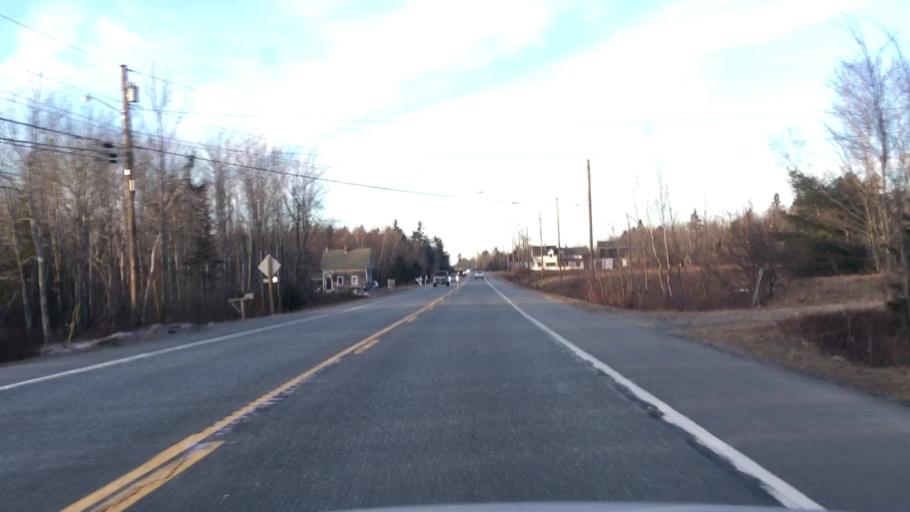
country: US
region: Maine
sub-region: Hancock County
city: Surry
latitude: 44.5945
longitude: -68.5110
